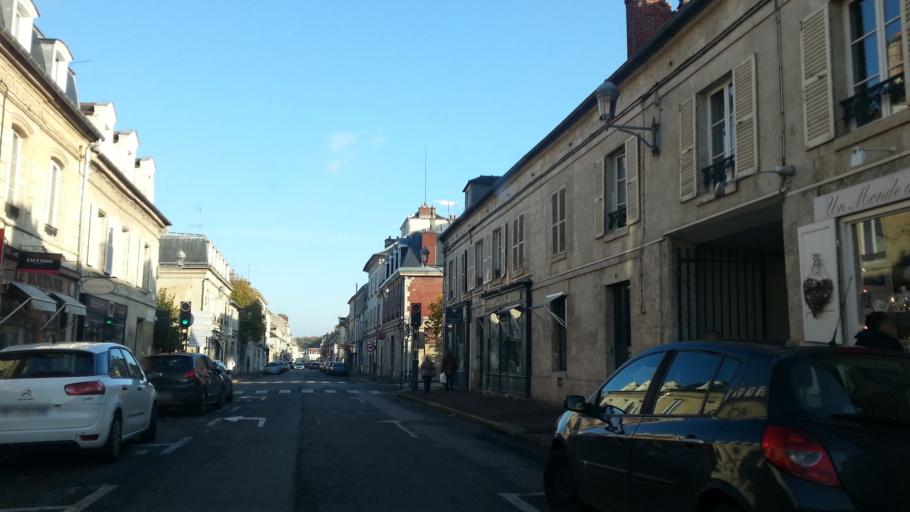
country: FR
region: Picardie
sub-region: Departement de l'Oise
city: Chantilly
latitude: 49.1943
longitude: 2.4705
